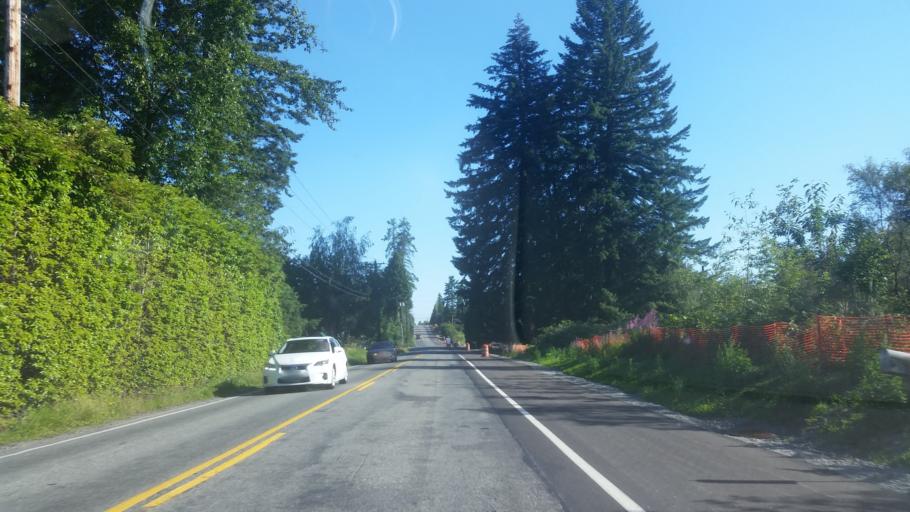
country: US
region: Washington
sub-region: Snohomish County
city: Maltby
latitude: 47.8220
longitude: -122.1099
